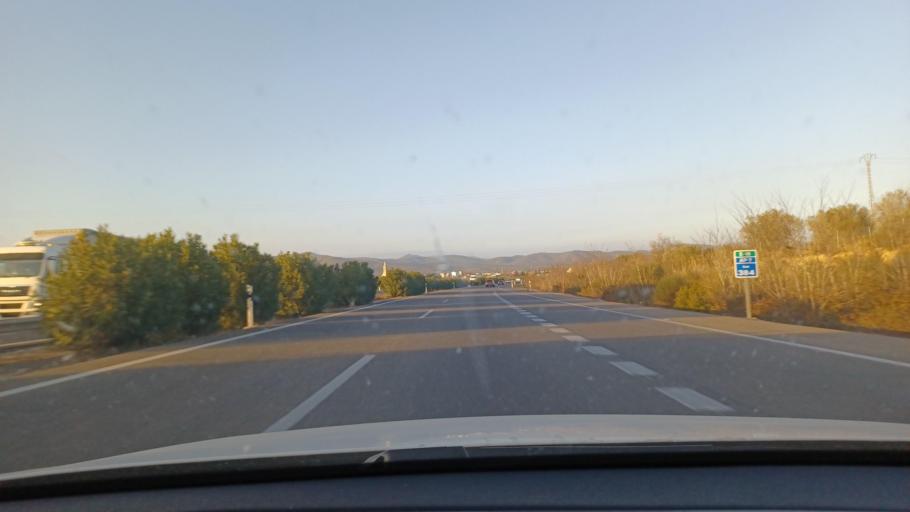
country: ES
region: Valencia
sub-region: Provincia de Castello
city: Alcala de Xivert
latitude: 40.2859
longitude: 0.2283
